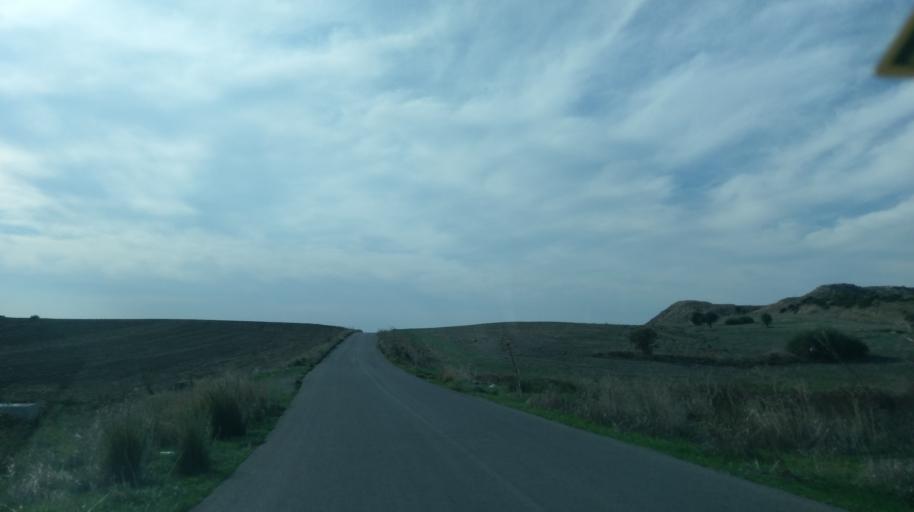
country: CY
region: Keryneia
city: Lapithos
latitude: 35.2812
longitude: 33.1950
